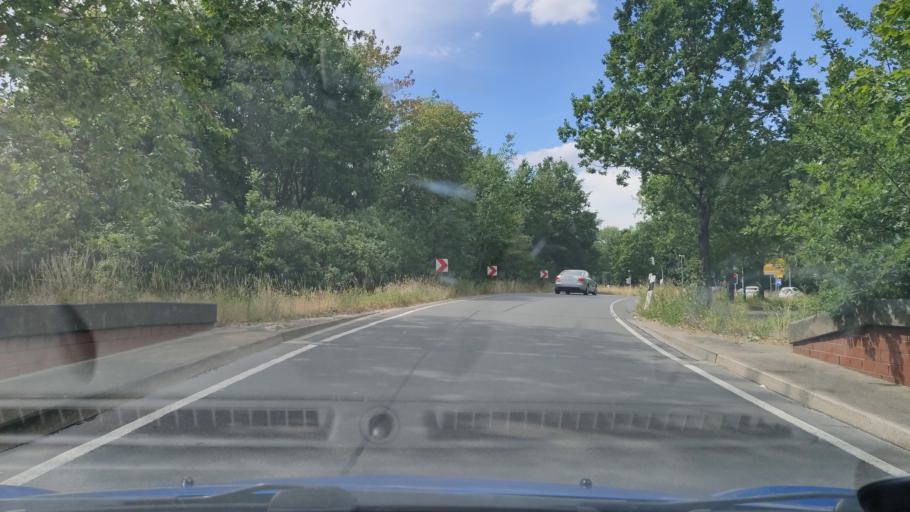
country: DE
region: Lower Saxony
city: Ronnenberg
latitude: 52.3480
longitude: 9.6741
